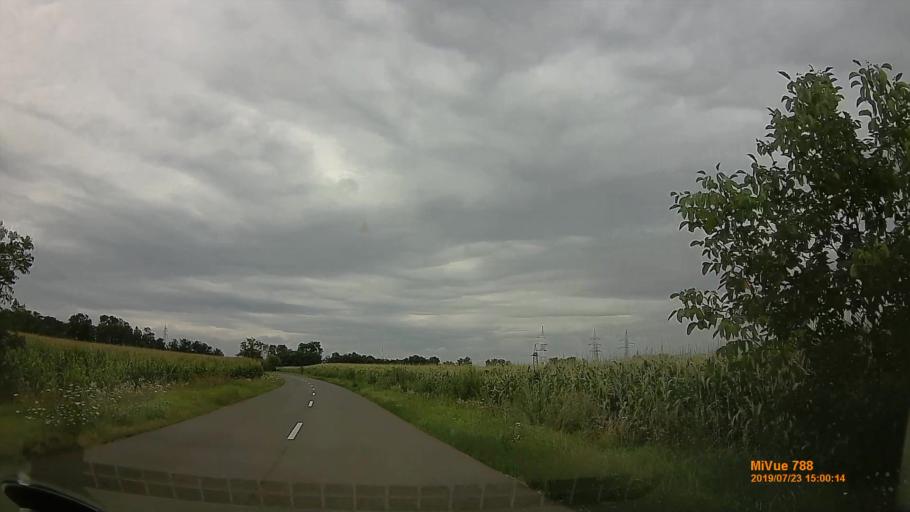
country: HU
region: Szabolcs-Szatmar-Bereg
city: Nyiregyhaza
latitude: 47.9274
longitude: 21.6771
